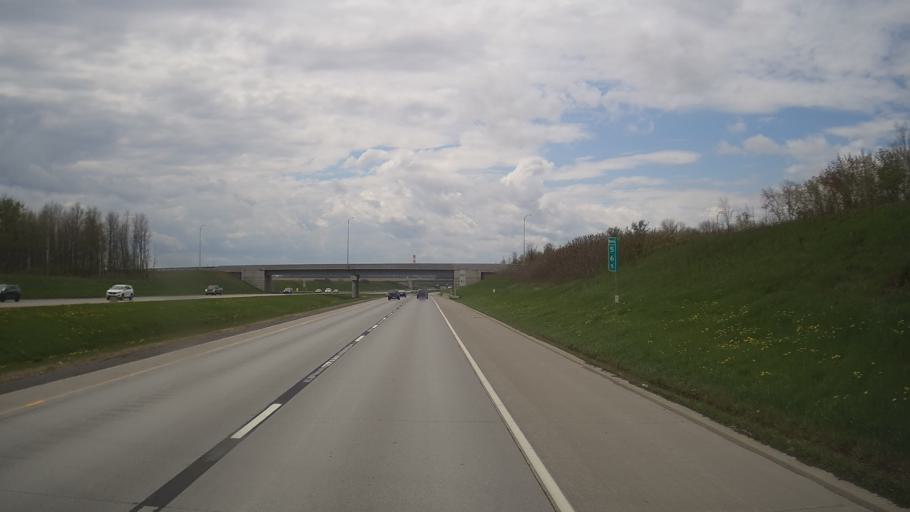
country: CA
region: Quebec
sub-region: Monteregie
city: Candiac
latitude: 45.3652
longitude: -73.5065
